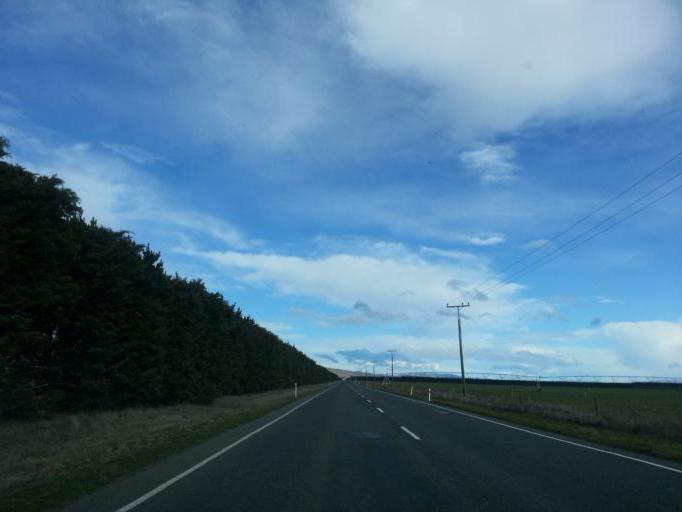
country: NZ
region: Canterbury
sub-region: Hurunui District
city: Amberley
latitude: -42.8041
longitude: 172.8241
